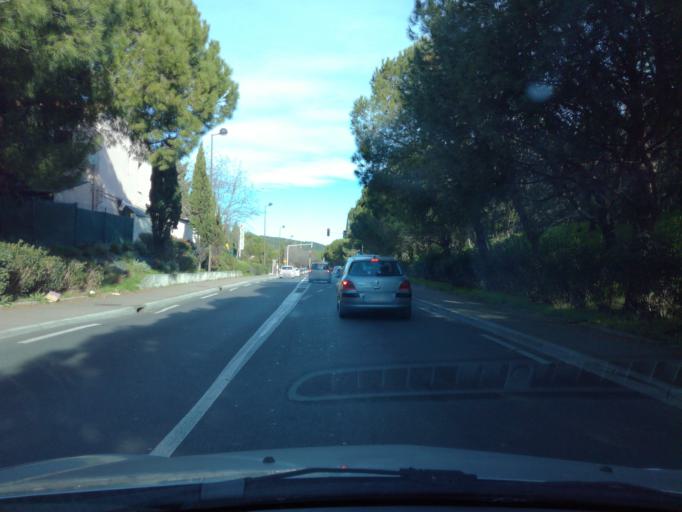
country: FR
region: Provence-Alpes-Cote d'Azur
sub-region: Departement des Alpes-Maritimes
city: Vallauris
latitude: 43.5755
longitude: 7.0902
